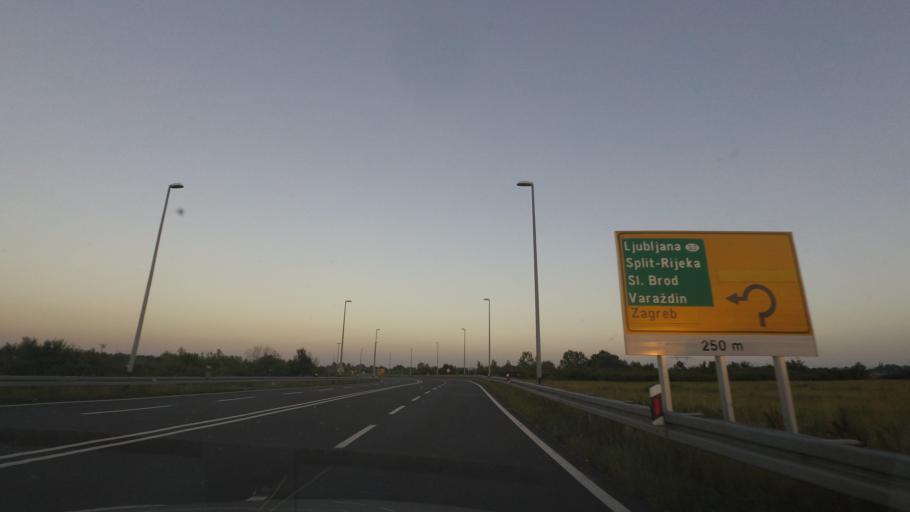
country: HR
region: Grad Zagreb
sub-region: Sesvete
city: Sesvete
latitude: 45.7904
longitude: 16.1601
